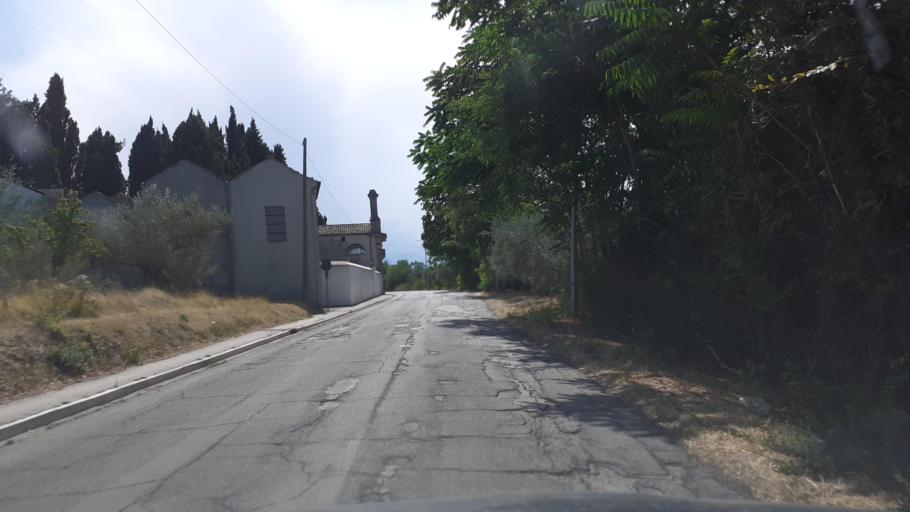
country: IT
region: Abruzzo
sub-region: Provincia di Chieti
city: Rocca San Giovanni
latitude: 42.2477
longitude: 14.4619
